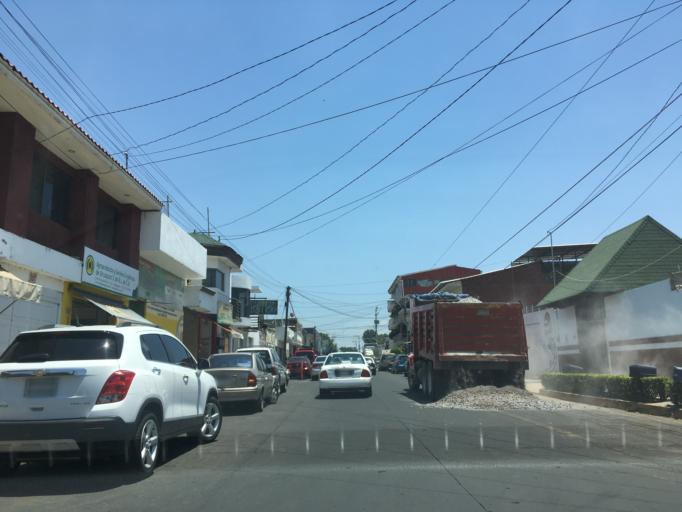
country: MX
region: Michoacan
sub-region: Uruapan
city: Uruapan
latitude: 19.4103
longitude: -102.0571
